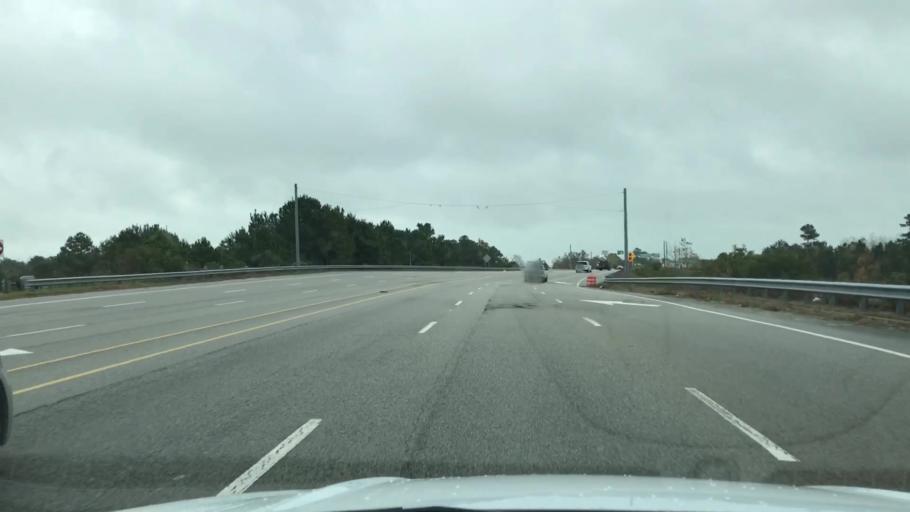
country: US
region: South Carolina
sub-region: Horry County
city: Myrtle Beach
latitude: 33.7556
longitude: -78.8541
